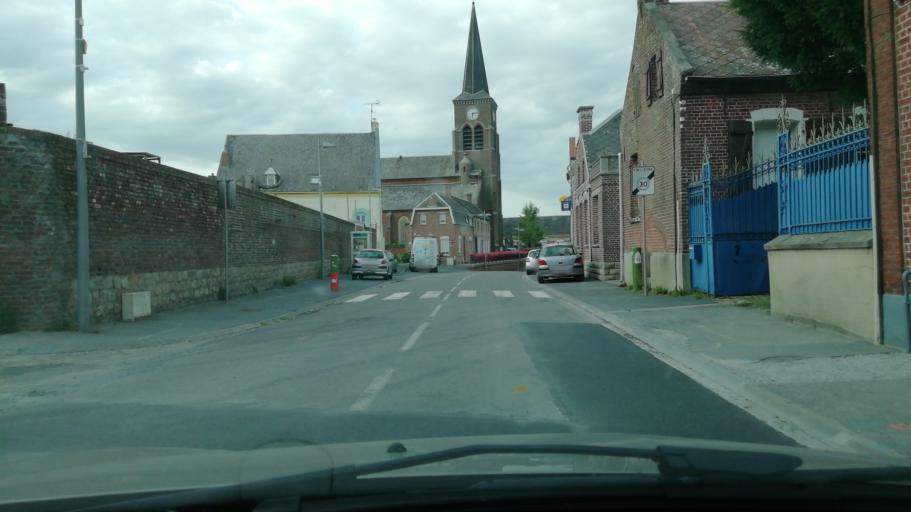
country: FR
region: Nord-Pas-de-Calais
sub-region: Departement du Nord
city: Saint-Hilaire-lez-Cambrai
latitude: 50.1828
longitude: 3.4137
